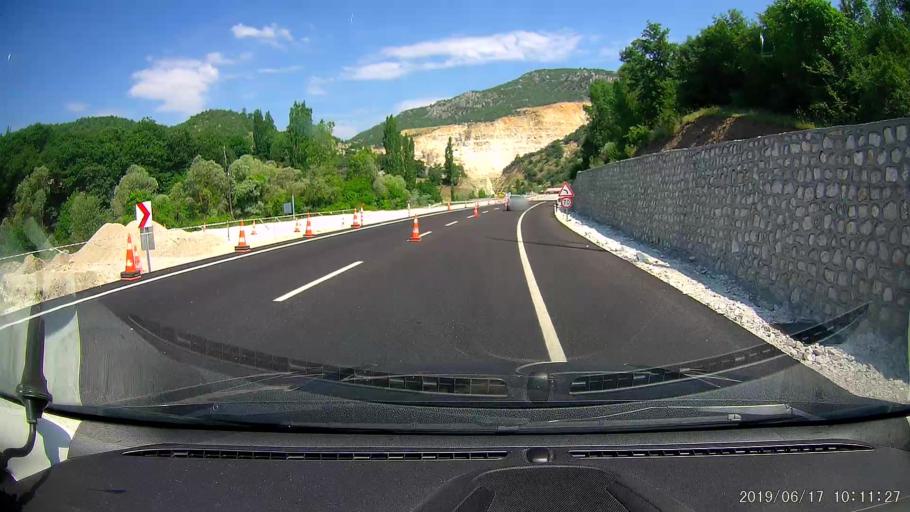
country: TR
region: Amasya
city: Saraycik
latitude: 40.9709
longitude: 35.0838
